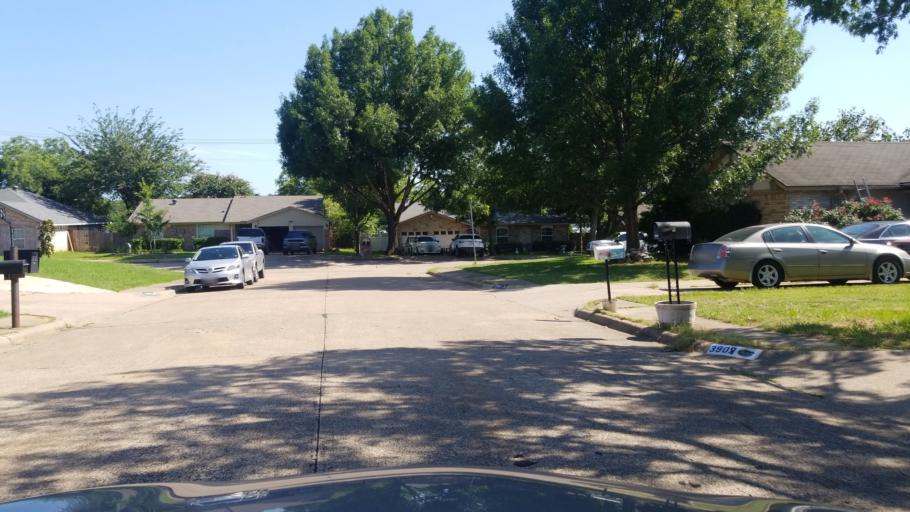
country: US
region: Texas
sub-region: Dallas County
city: Grand Prairie
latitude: 32.6775
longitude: -97.0134
